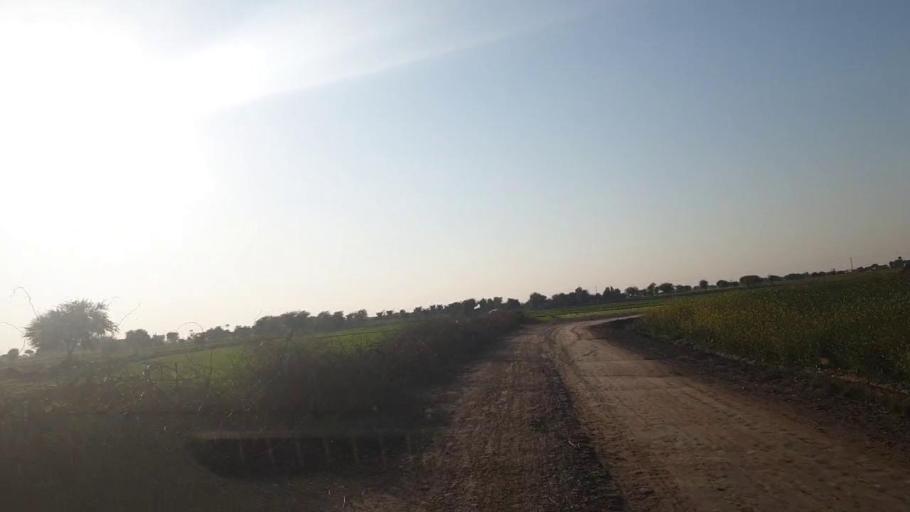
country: PK
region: Sindh
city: Shahpur Chakar
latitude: 26.0670
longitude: 68.6492
